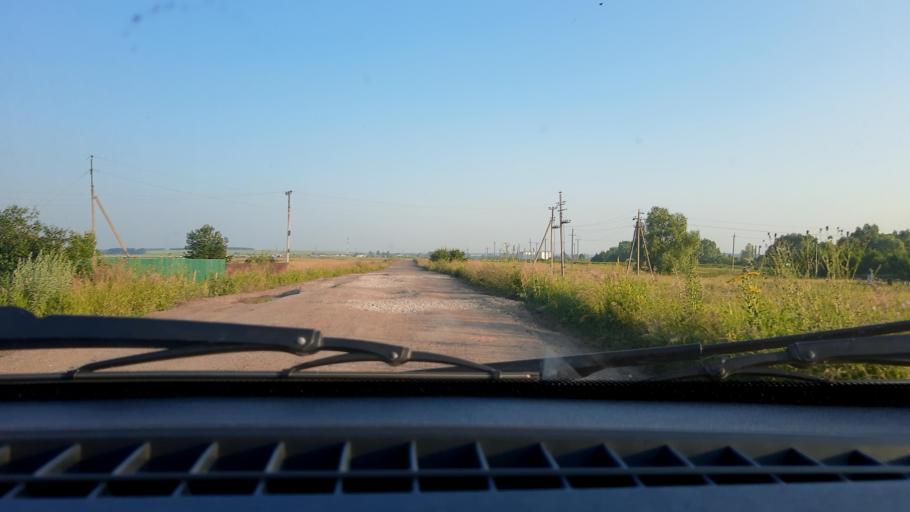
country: RU
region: Bashkortostan
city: Asanovo
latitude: 54.9145
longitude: 55.6271
